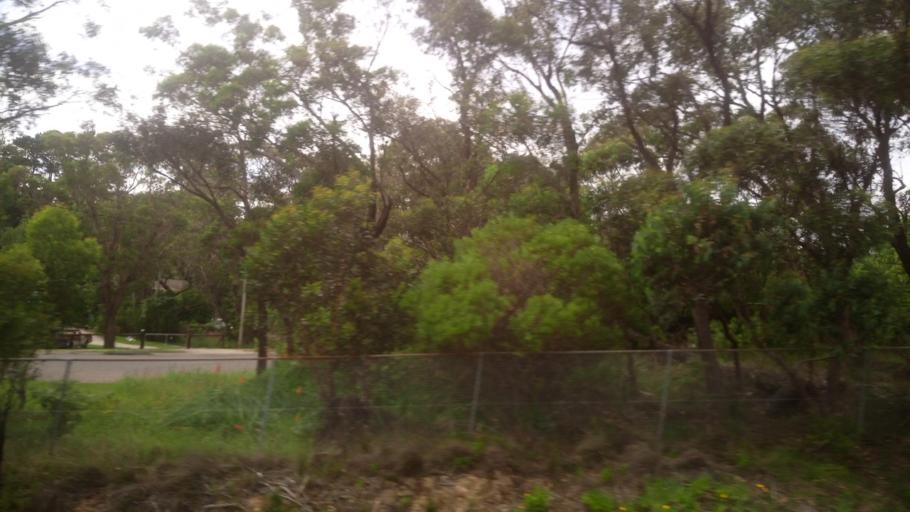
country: AU
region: New South Wales
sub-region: Blue Mountains Municipality
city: Leura
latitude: -33.7094
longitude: 150.3649
